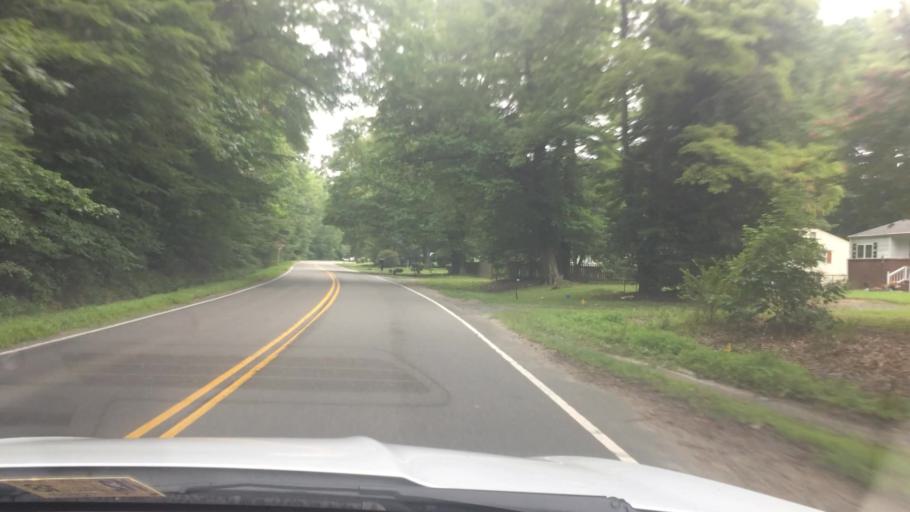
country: US
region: Virginia
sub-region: York County
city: Yorktown
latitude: 37.2275
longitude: -76.5238
